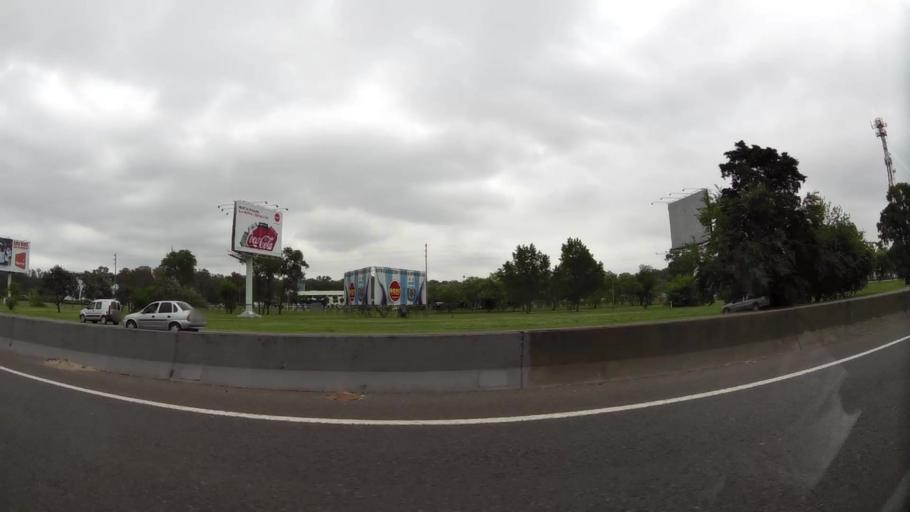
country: AR
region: Buenos Aires
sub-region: Partido de Ezeiza
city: Ezeiza
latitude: -34.7752
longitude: -58.5244
